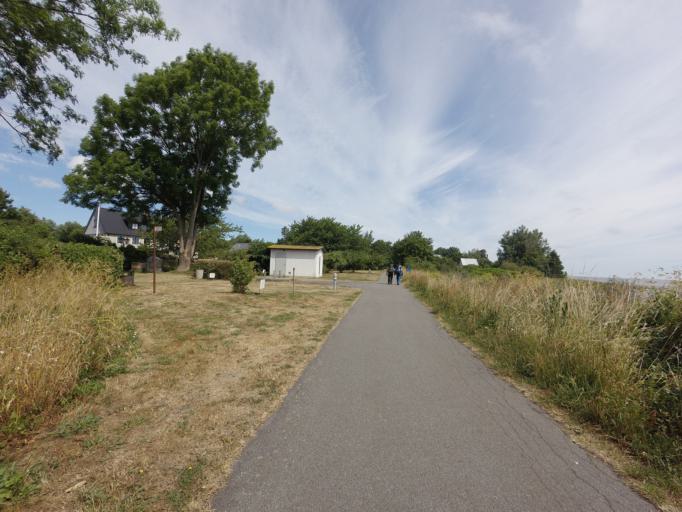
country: SE
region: Skane
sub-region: Simrishamns Kommun
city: Simrishamn
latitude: 55.5255
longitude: 14.3481
